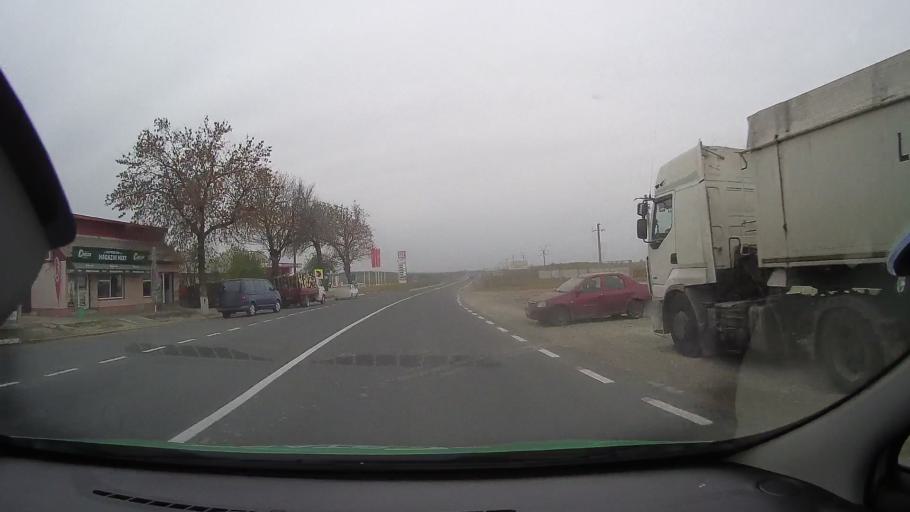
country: RO
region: Constanta
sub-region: Oras Harsova
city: Harsova
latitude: 44.6912
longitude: 27.9400
